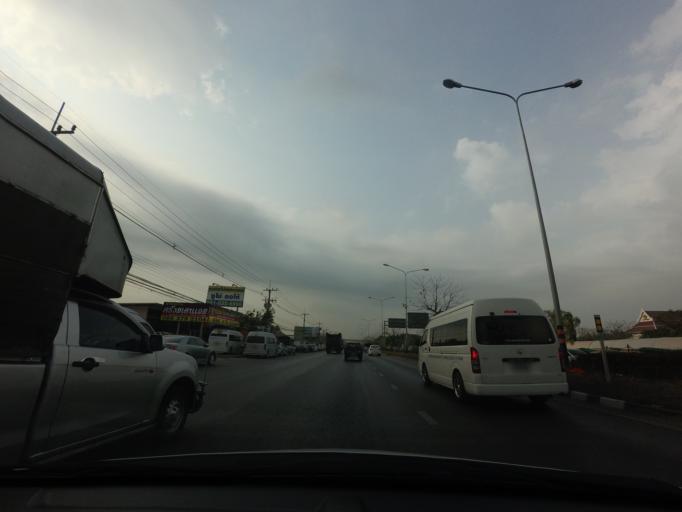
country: TH
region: Bangkok
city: Thawi Watthana
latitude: 13.7721
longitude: 100.3283
